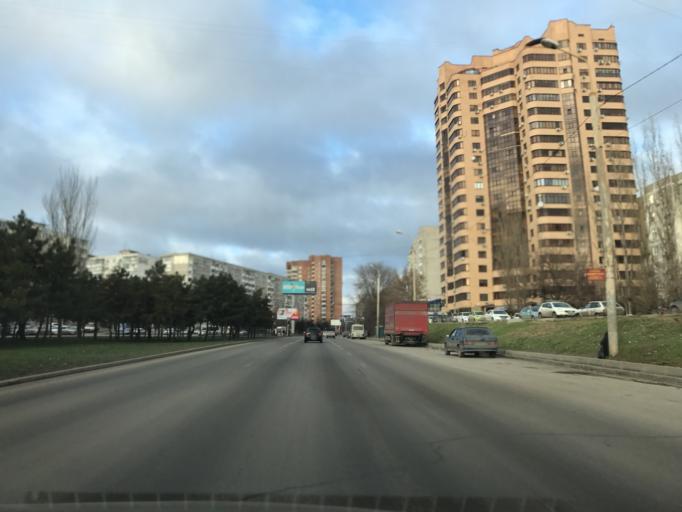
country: RU
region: Rostov
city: Severnyy
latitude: 47.2902
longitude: 39.6951
